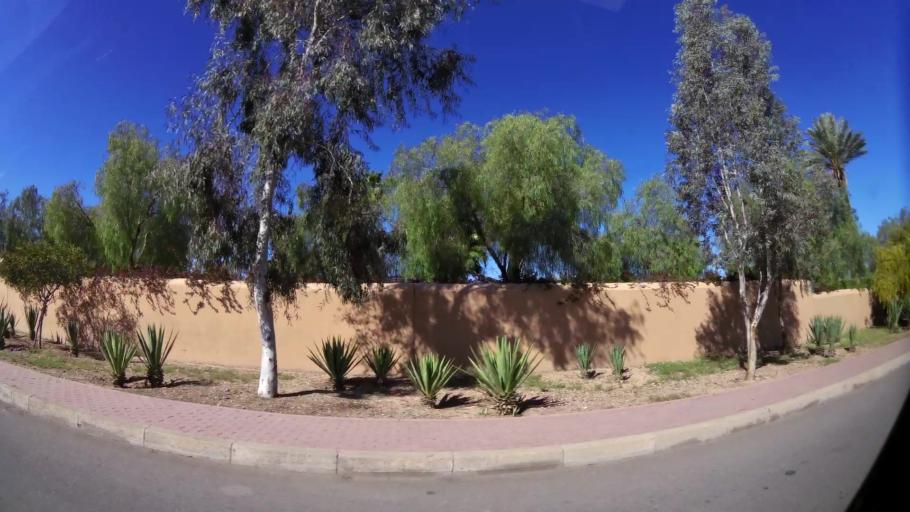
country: MA
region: Marrakech-Tensift-Al Haouz
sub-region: Marrakech
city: Marrakesh
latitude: 31.6493
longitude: -7.9354
